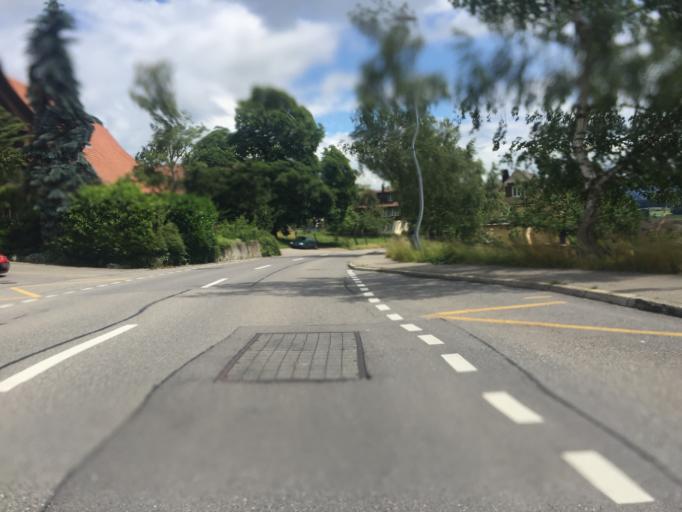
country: CH
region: Bern
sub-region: Bern-Mittelland District
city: Kirchlindach
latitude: 46.9877
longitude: 7.3869
